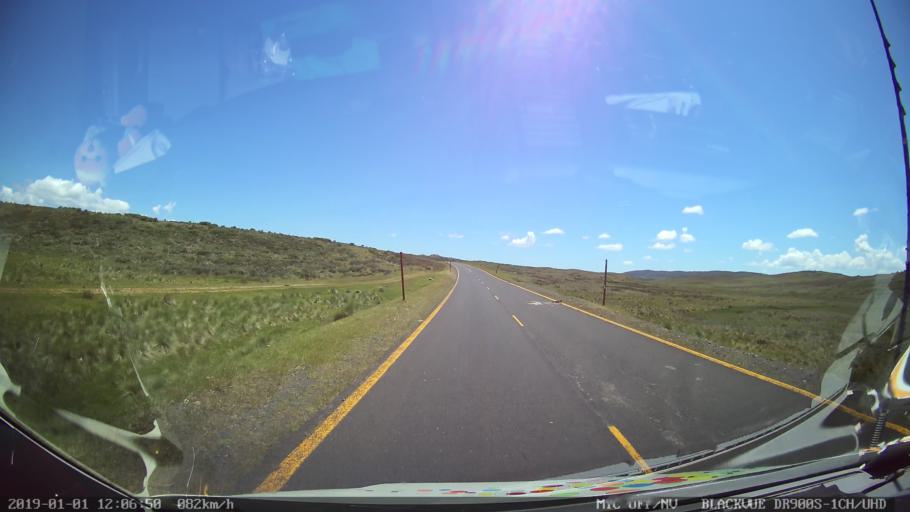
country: AU
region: New South Wales
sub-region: Snowy River
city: Jindabyne
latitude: -35.8403
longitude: 148.4911
